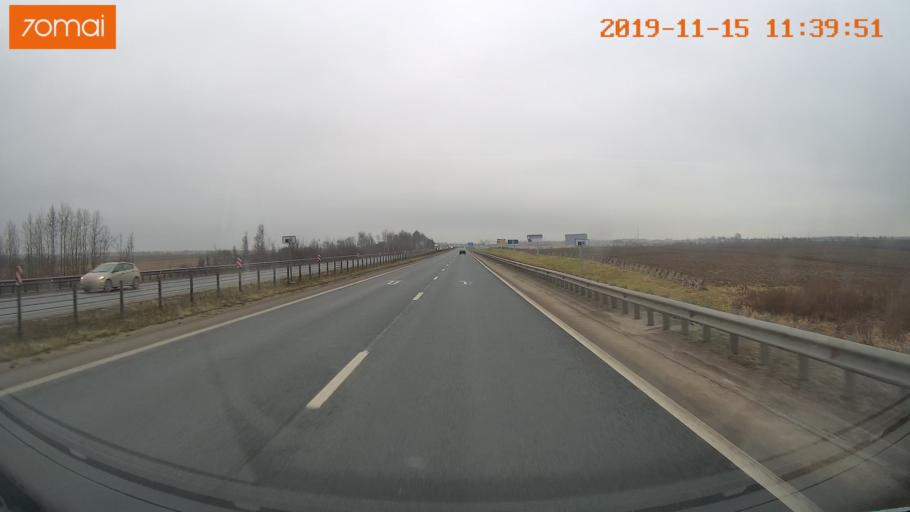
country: RU
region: Vologda
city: Molochnoye
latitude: 59.2119
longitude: 39.7354
